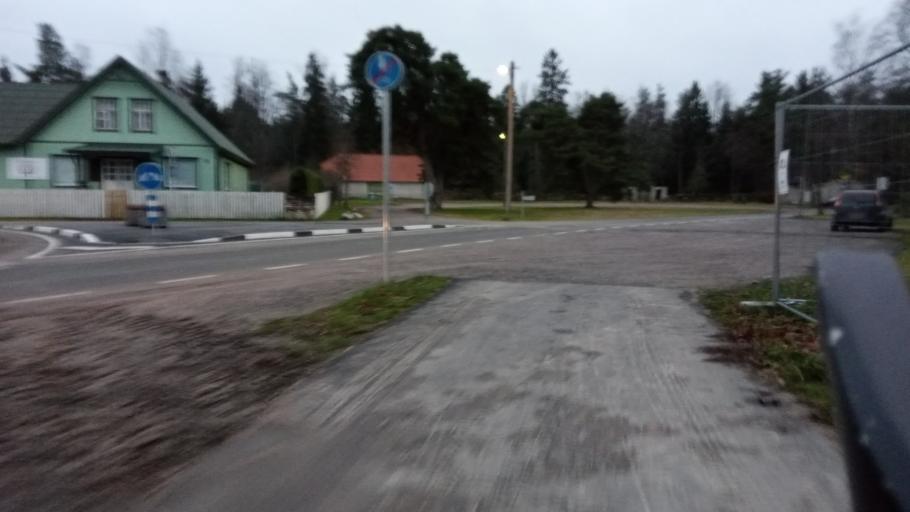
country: EE
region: Harju
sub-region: Kuusalu vald
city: Kuusalu
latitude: 59.4458
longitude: 25.4469
